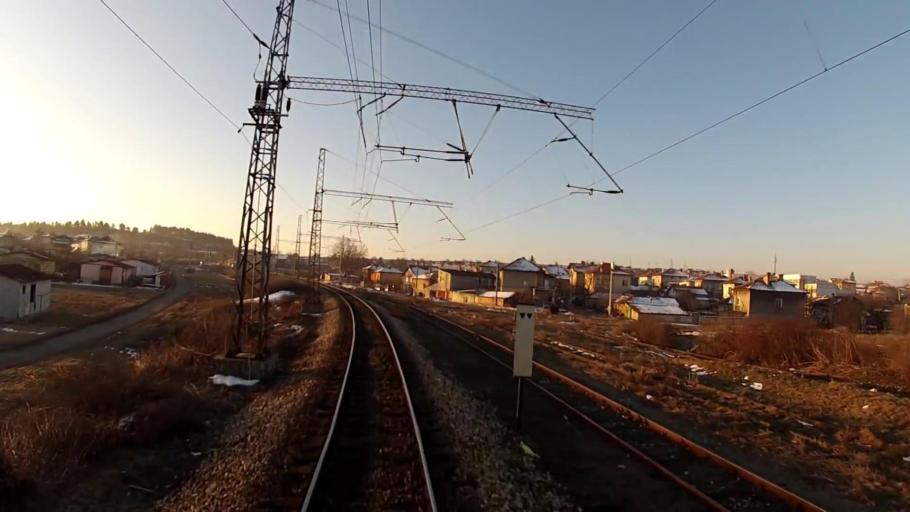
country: BG
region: Sofiya
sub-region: Obshtina Dragoman
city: Dragoman
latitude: 42.9155
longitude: 22.9347
